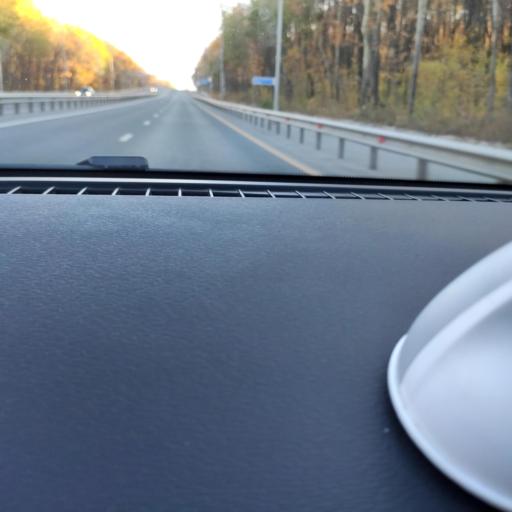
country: RU
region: Samara
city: Petra-Dubrava
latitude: 53.2884
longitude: 50.2490
